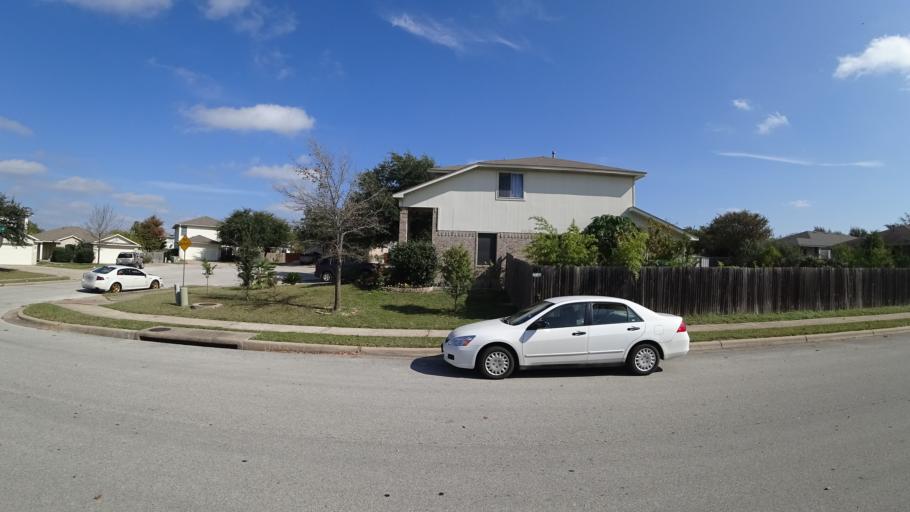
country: US
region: Texas
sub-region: Travis County
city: Pflugerville
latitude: 30.4177
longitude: -97.6381
